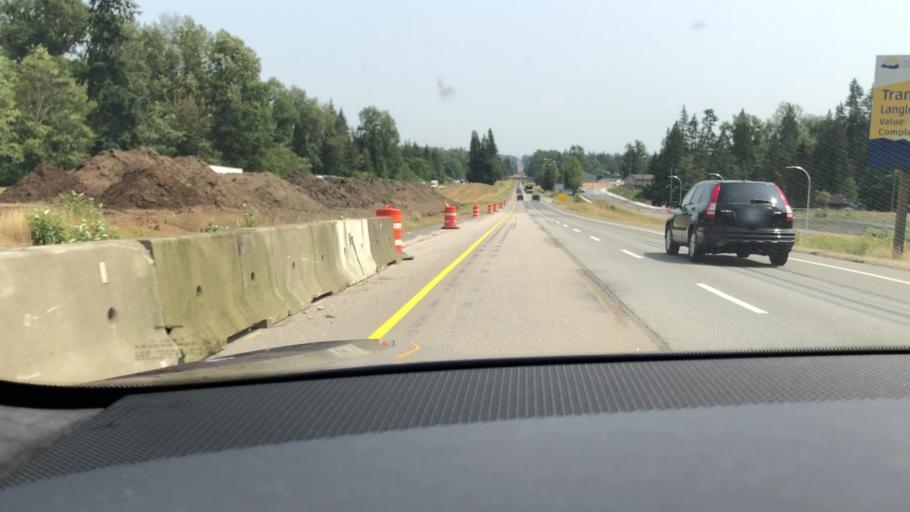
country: CA
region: British Columbia
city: Walnut Grove
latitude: 49.1480
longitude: -122.6118
